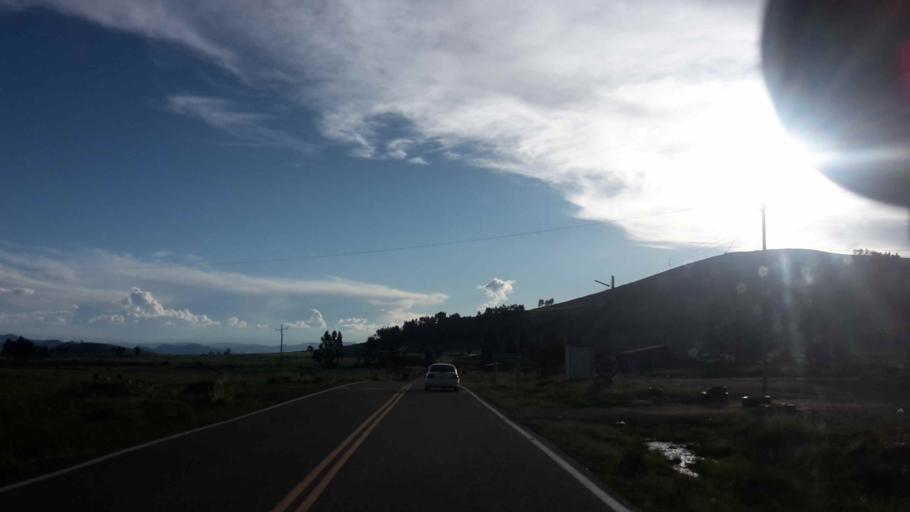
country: BO
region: Cochabamba
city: Arani
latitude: -17.5506
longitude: -65.6869
